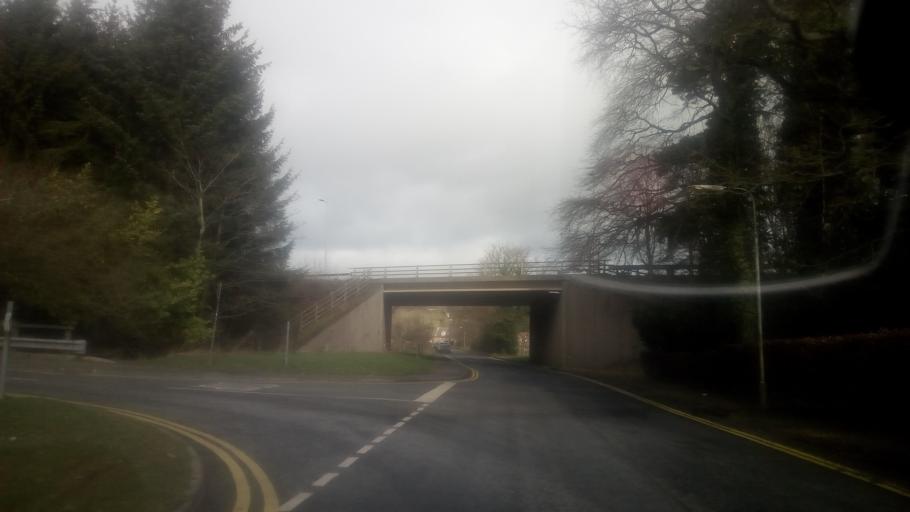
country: GB
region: Scotland
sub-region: The Scottish Borders
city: Melrose
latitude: 55.5965
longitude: -2.7391
